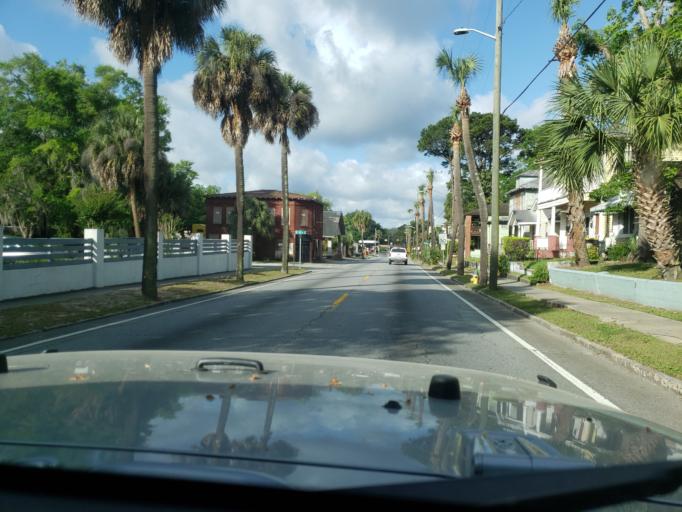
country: US
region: Georgia
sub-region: Chatham County
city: Savannah
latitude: 32.0598
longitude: -81.1124
